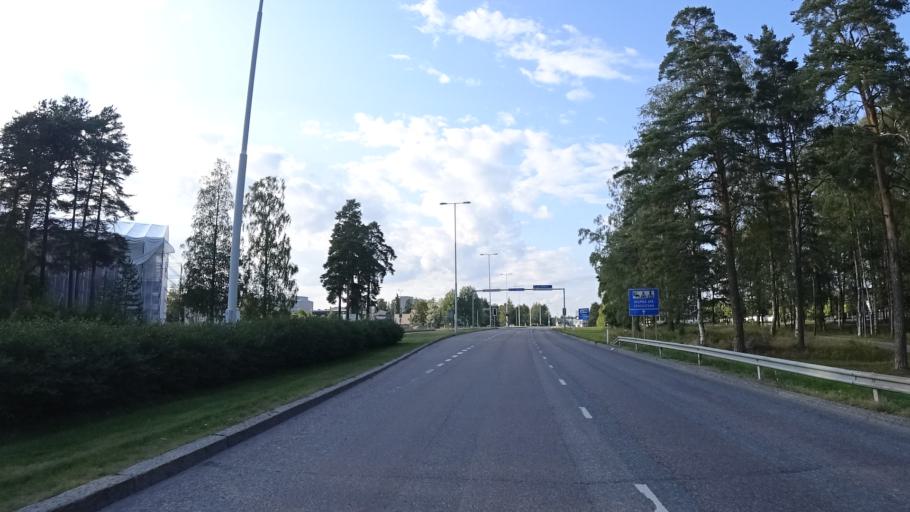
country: FI
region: South Karelia
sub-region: Imatra
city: Imatra
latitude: 61.1836
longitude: 28.7798
